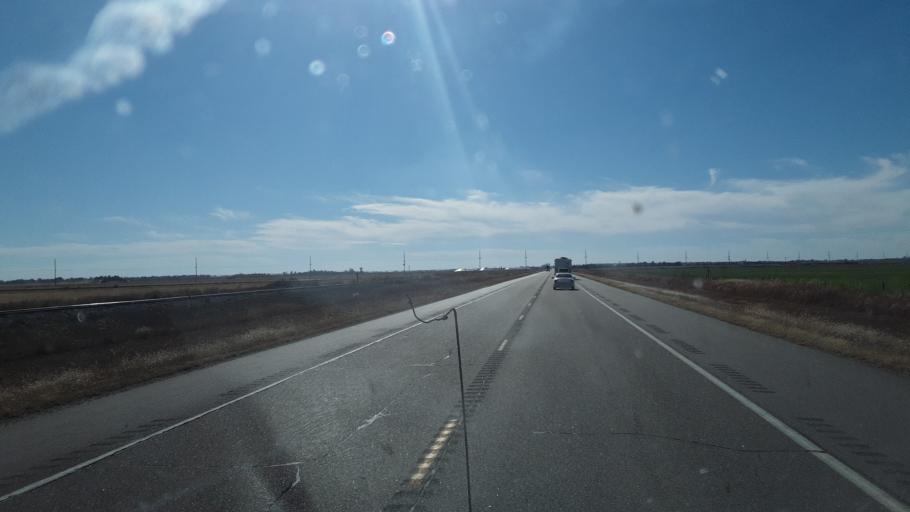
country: US
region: Kansas
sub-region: Pawnee County
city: Larned
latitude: 38.2221
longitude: -99.0428
